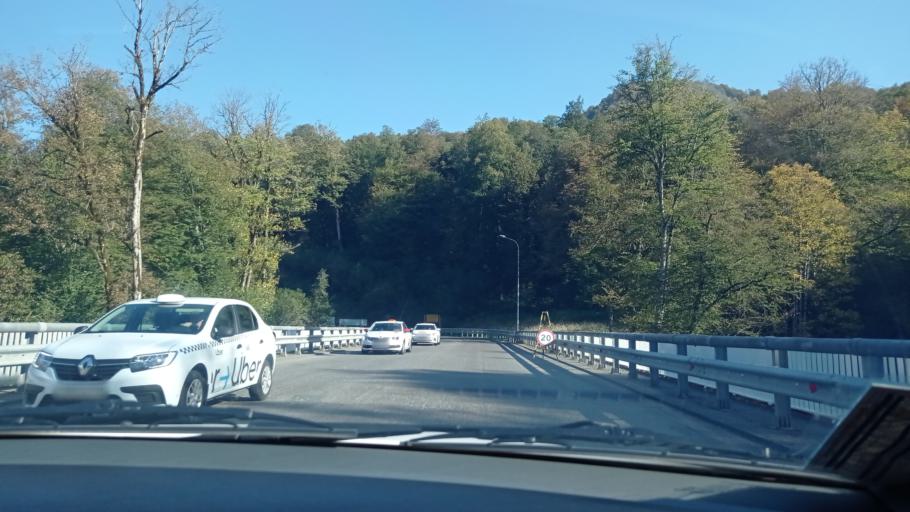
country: RU
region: Krasnodarskiy
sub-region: Sochi City
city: Krasnaya Polyana
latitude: 43.6589
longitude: 40.3017
